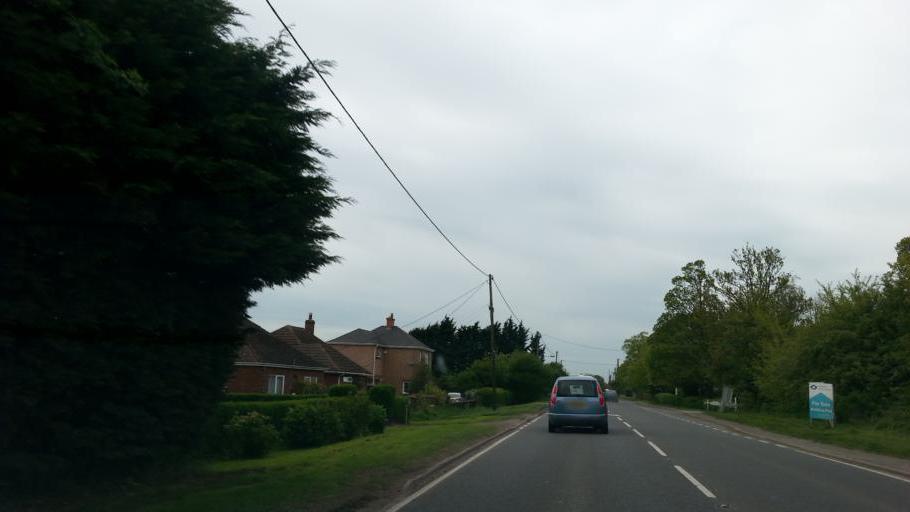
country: GB
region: England
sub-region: Cambridgeshire
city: March
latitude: 52.5638
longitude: 0.0639
